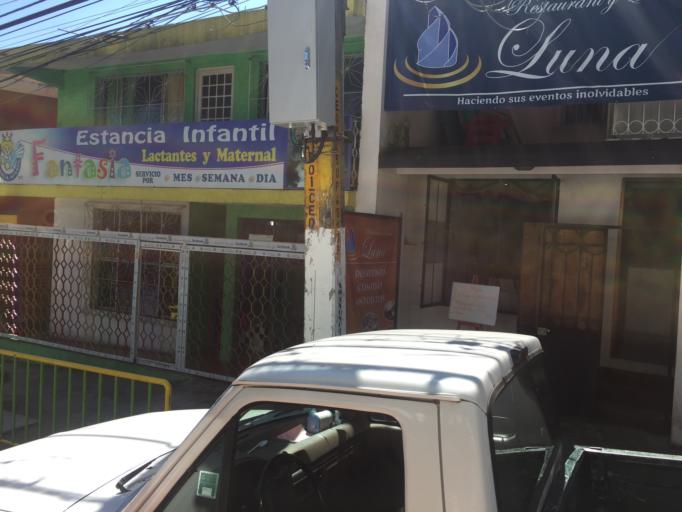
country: MX
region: Veracruz
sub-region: Xalapa
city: Xalapa de Enriquez
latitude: 19.5393
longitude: -96.9188
